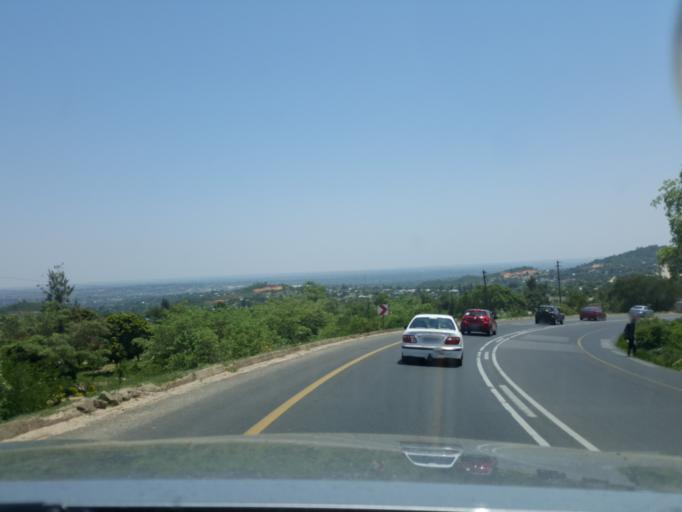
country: ZA
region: Limpopo
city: Thulamahashi
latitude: -24.8287
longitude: 31.0819
